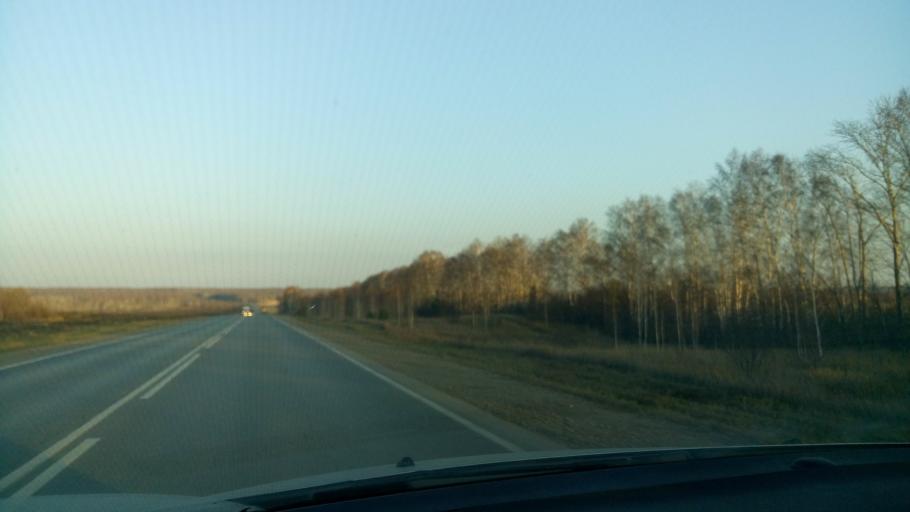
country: RU
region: Sverdlovsk
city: Yelanskiy
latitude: 56.7590
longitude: 62.3614
